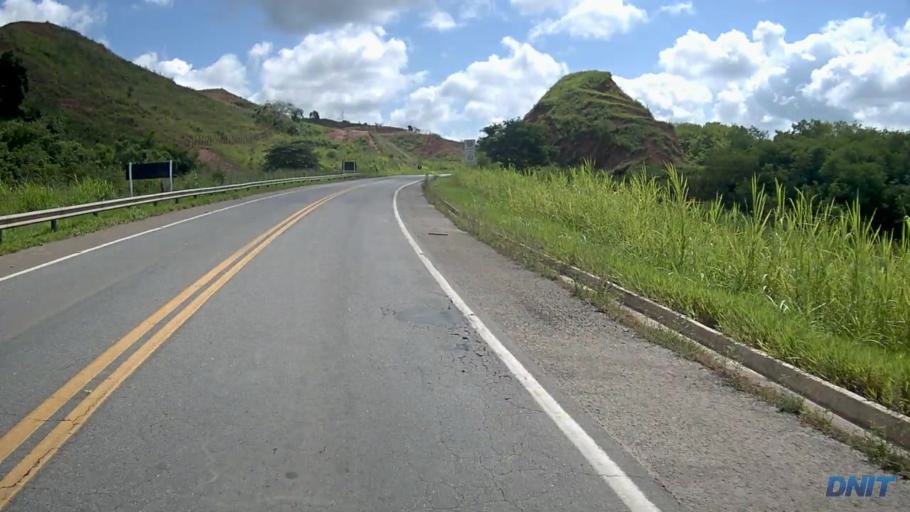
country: BR
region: Minas Gerais
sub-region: Belo Oriente
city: Belo Oriente
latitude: -19.1467
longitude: -42.2311
